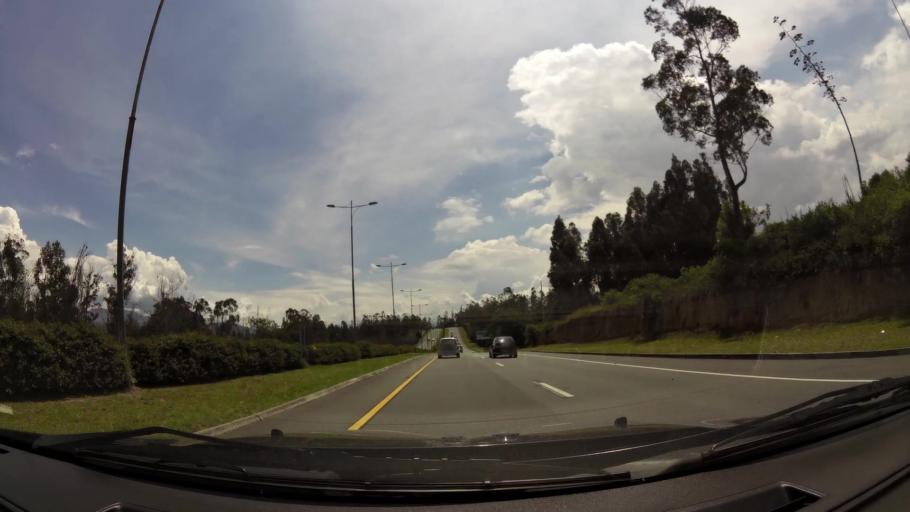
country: EC
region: Pichincha
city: Quito
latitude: -0.1741
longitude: -78.3432
